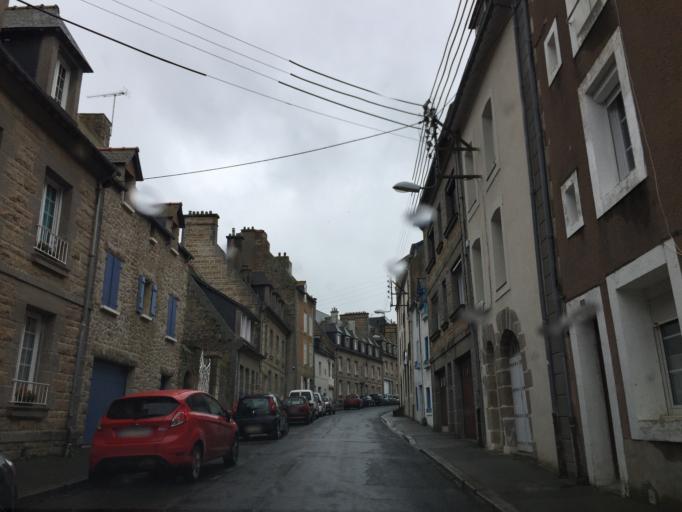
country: FR
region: Brittany
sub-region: Departement d'Ille-et-Vilaine
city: Saint-Malo
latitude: 48.6362
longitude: -2.0247
